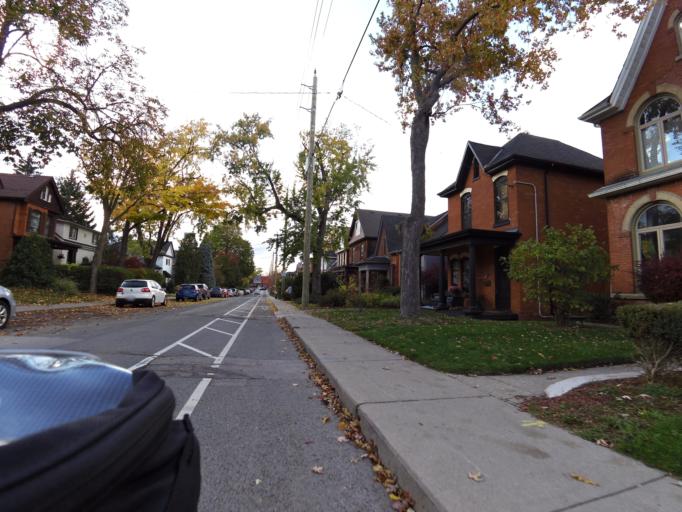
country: CA
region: Ontario
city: Hamilton
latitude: 43.2537
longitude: -79.8880
